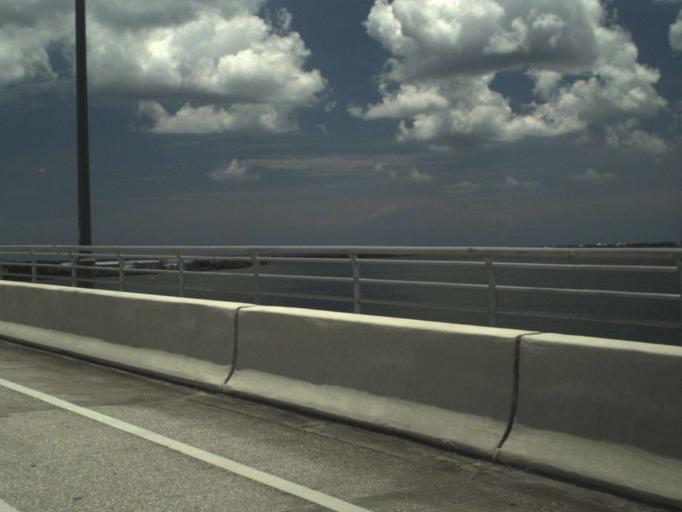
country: US
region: Florida
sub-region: Martin County
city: Sewall's Point
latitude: 27.2063
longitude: -80.1929
